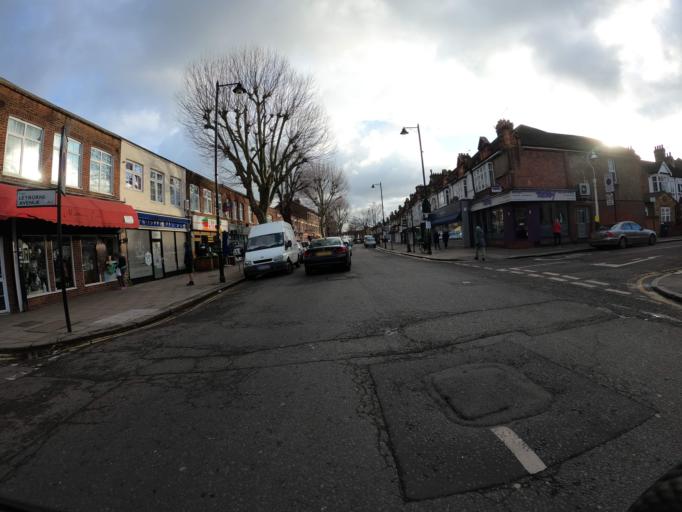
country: GB
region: England
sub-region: Greater London
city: Ealing
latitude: 51.5029
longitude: -0.3167
